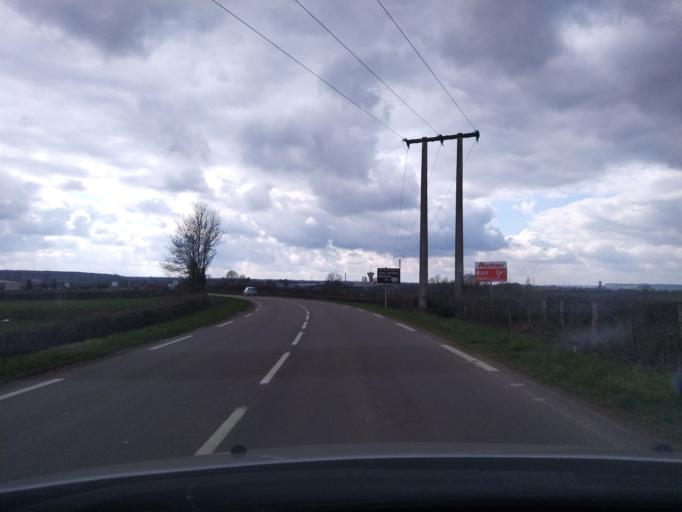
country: FR
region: Bourgogne
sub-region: Departement de l'Yonne
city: Avallon
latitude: 47.5058
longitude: 3.9297
